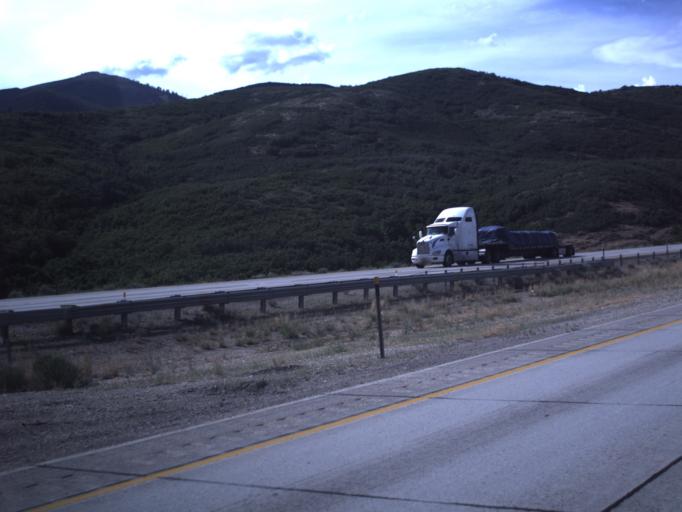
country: US
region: Utah
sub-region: Wasatch County
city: Heber
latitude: 40.5857
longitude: -111.4364
